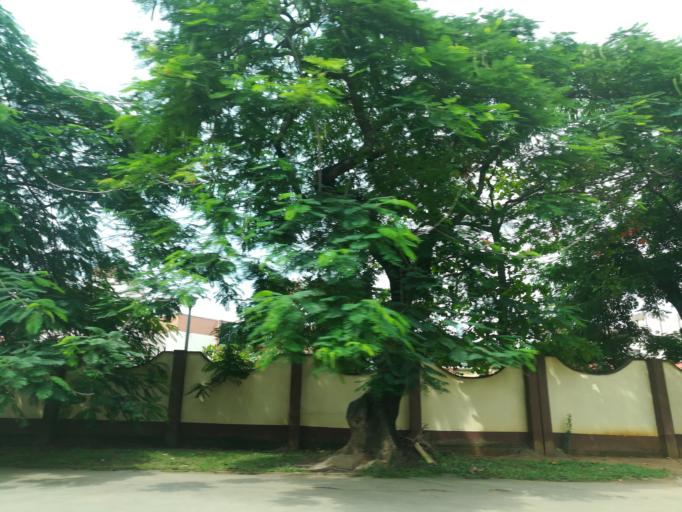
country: NG
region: Lagos
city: Ikeja
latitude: 6.6164
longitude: 3.3625
